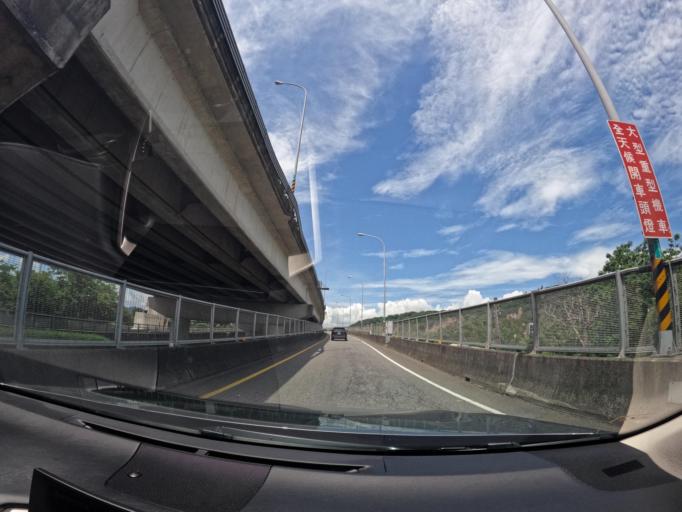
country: TW
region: Taiwan
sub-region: Miaoli
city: Miaoli
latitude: 24.5336
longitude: 120.8155
